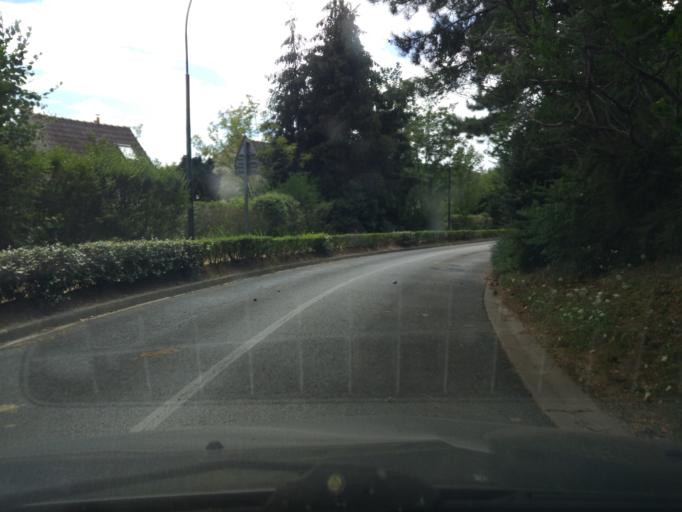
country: FR
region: Ile-de-France
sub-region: Departement de l'Essonne
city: Villiers-le-Bacle
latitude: 48.7061
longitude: 2.1204
